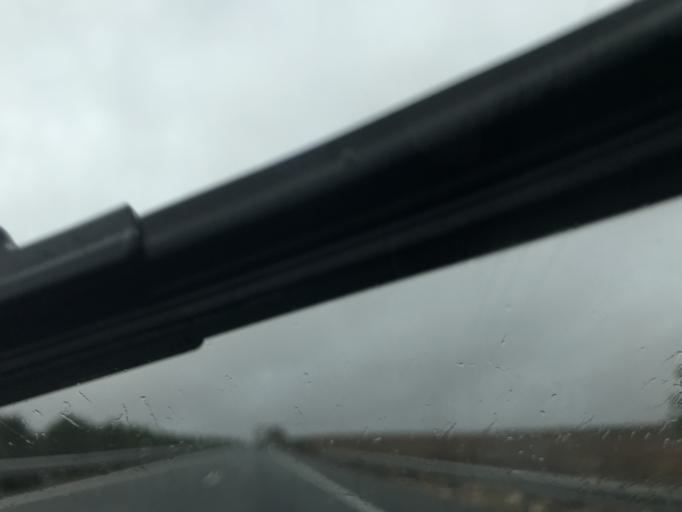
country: ES
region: Andalusia
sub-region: Provincia de Malaga
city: Fuente de Piedra
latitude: 37.1628
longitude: -4.7526
